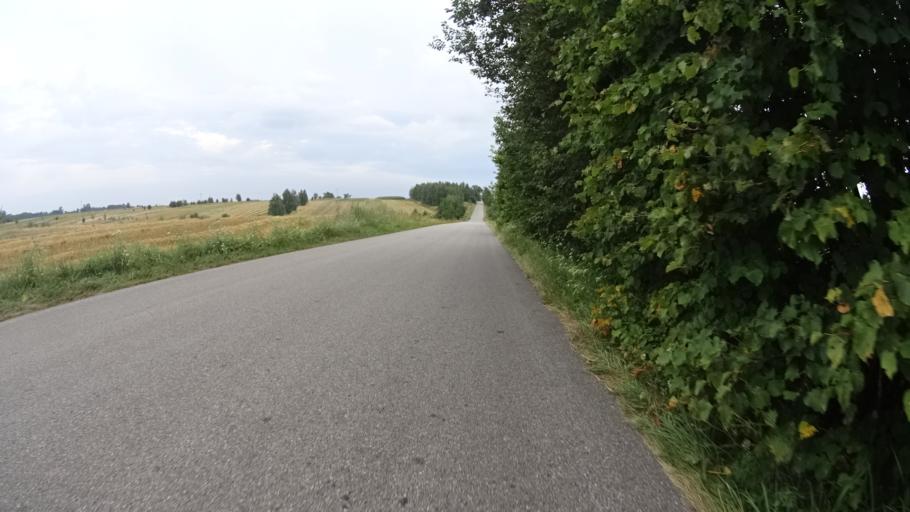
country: PL
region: Masovian Voivodeship
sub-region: Powiat grojecki
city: Goszczyn
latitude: 51.6732
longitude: 20.8579
